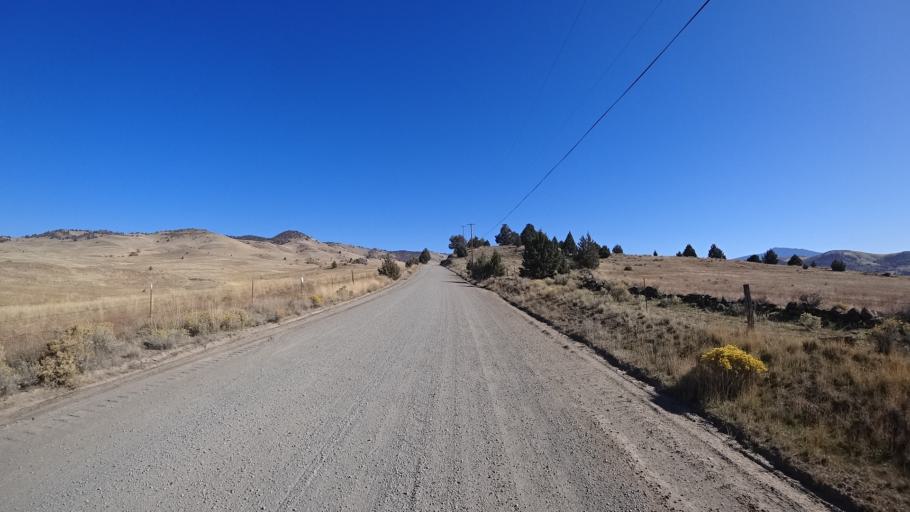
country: US
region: California
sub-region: Siskiyou County
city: Montague
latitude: 41.8324
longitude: -122.3791
